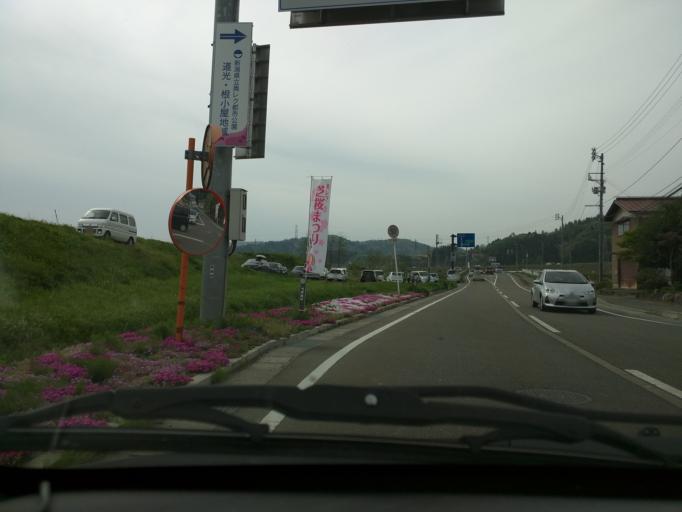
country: JP
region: Niigata
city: Ojiya
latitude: 37.2538
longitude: 138.9213
